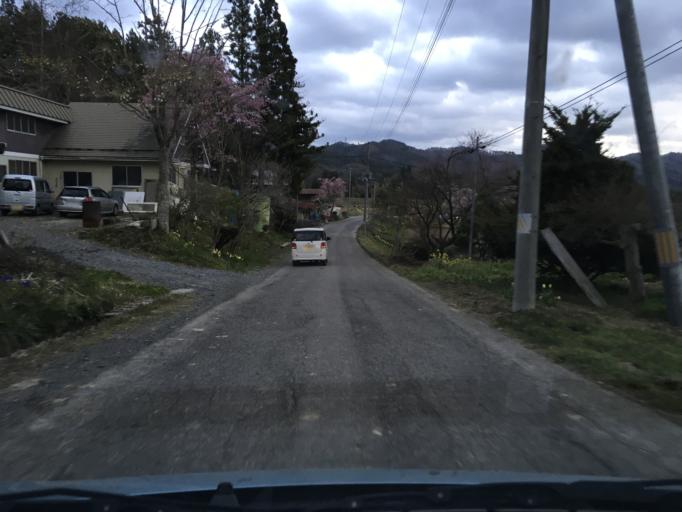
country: JP
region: Iwate
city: Ichinoseki
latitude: 38.9700
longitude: 141.2142
